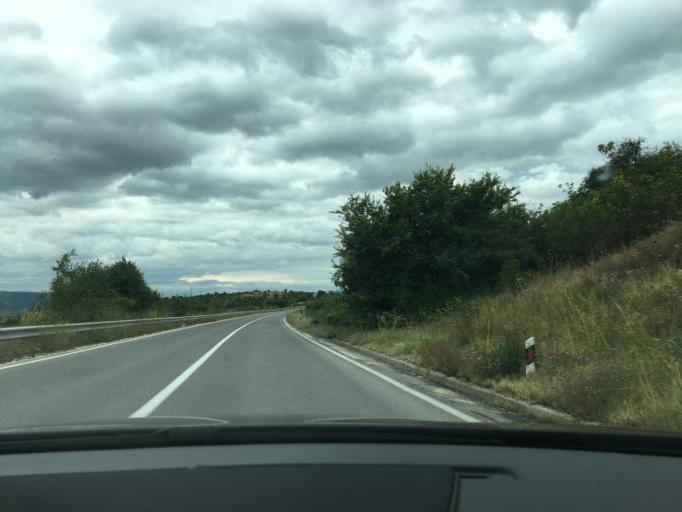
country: MK
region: Opstina Rankovce
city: Rankovce
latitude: 42.1489
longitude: 22.0264
